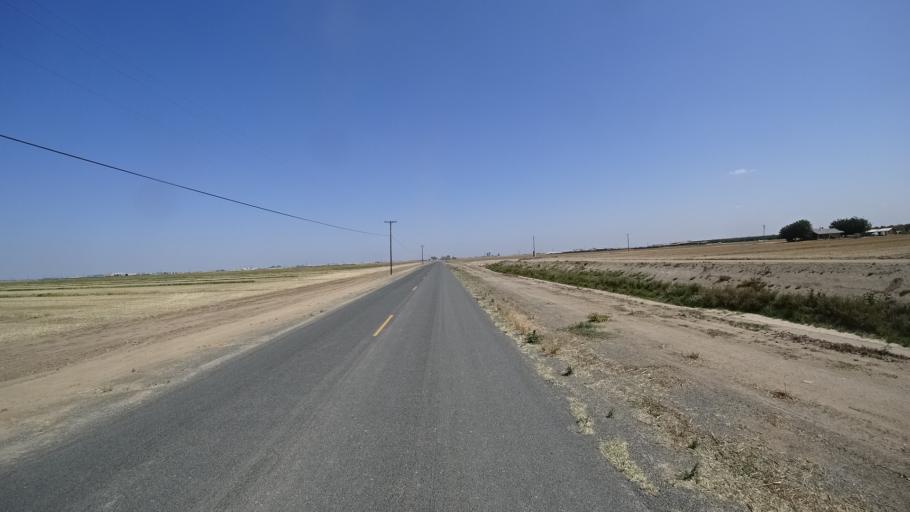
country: US
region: California
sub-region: Kings County
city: Home Garden
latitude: 36.2458
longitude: -119.6189
